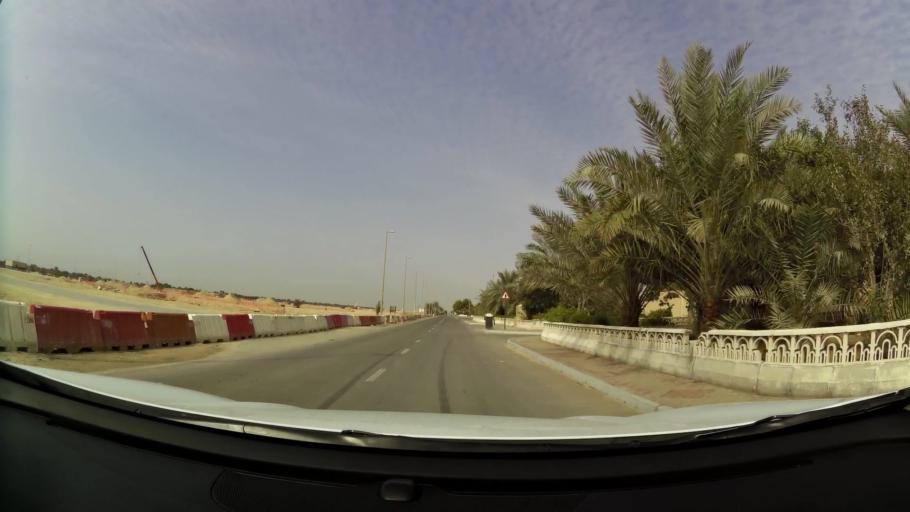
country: AE
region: Abu Dhabi
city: Abu Dhabi
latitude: 24.5962
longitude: 54.6948
